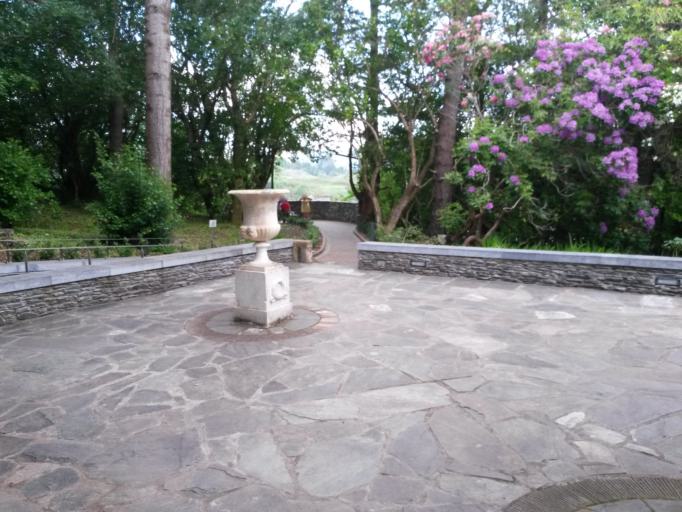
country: IE
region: Munster
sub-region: County Cork
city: Bantry
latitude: 51.7374
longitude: -9.5435
